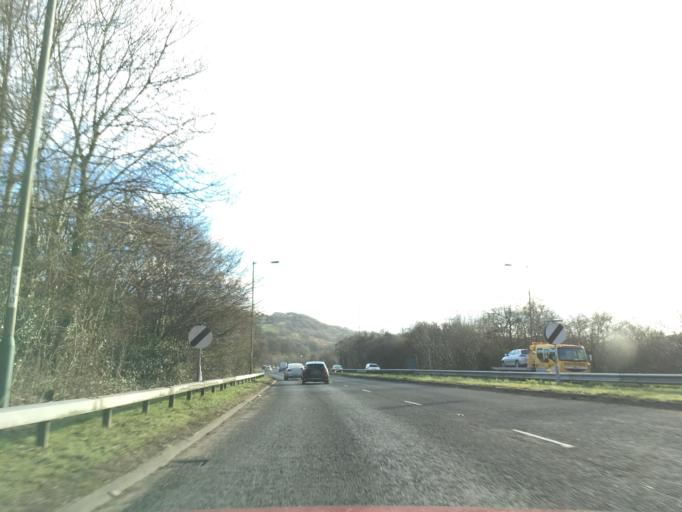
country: GB
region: Wales
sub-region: Caerphilly County Borough
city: Maesycwmmer
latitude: 51.6320
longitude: -3.2298
